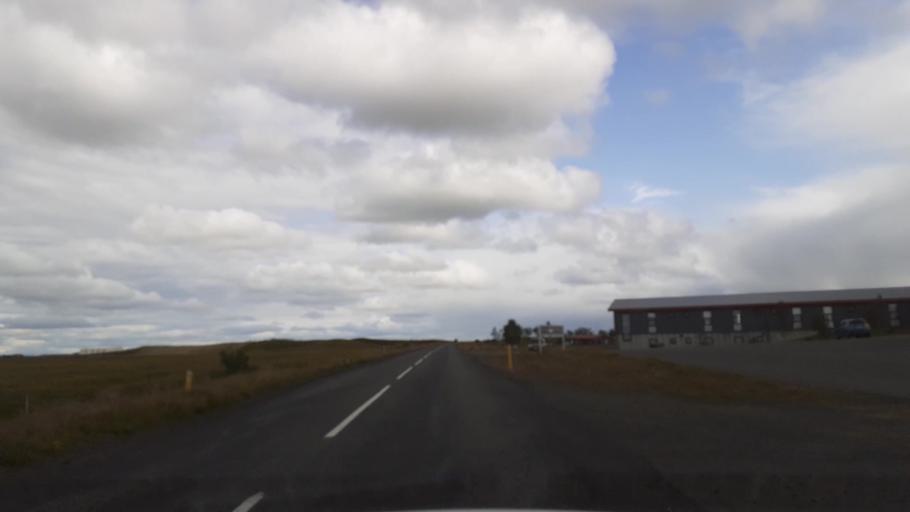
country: IS
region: South
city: Vestmannaeyjar
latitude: 63.8312
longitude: -20.4228
